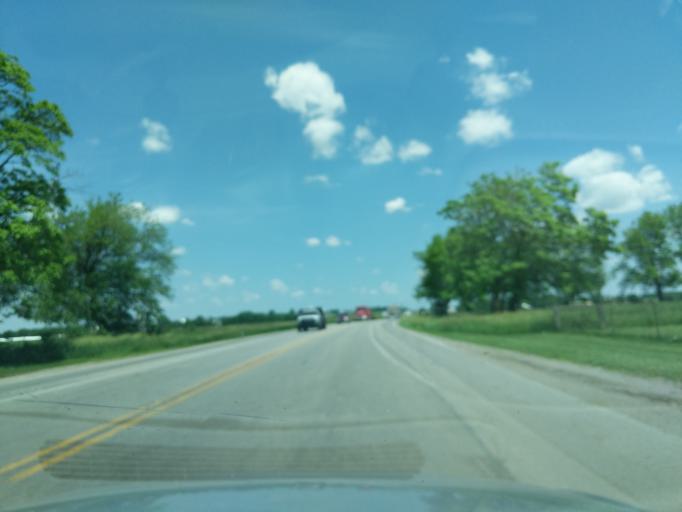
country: US
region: Indiana
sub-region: LaGrange County
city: Topeka
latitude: 41.6112
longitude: -85.5793
